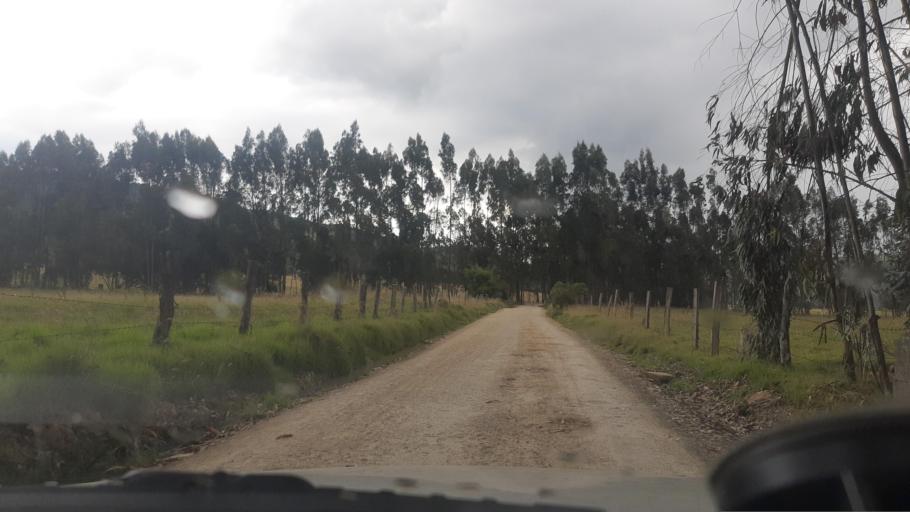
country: CO
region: Cundinamarca
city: Cucunuba
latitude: 5.1814
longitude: -73.8003
